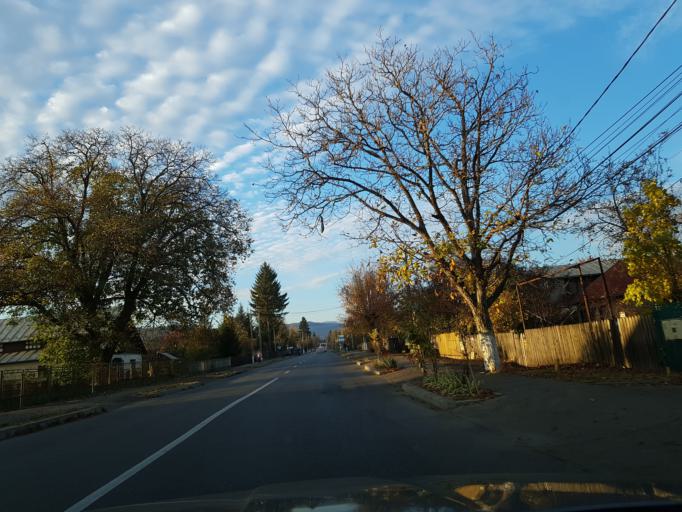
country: RO
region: Prahova
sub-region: Oras Breaza
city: Breaza
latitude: 45.1870
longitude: 25.6620
